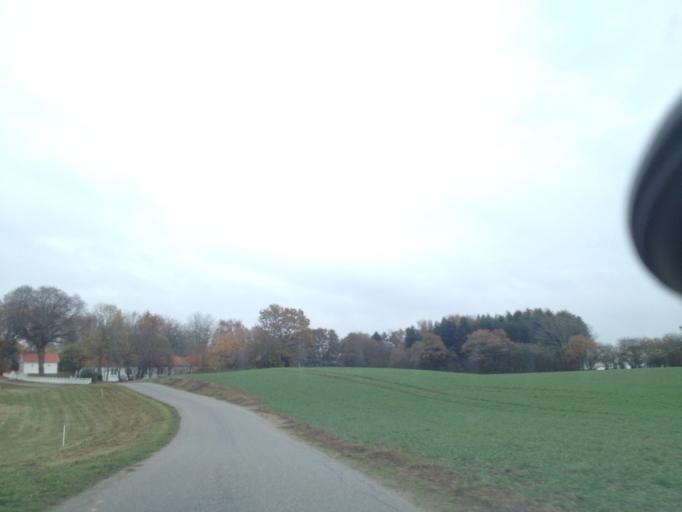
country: DK
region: South Denmark
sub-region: Nordfyns Kommune
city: Sonderso
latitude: 55.4240
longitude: 10.2138
